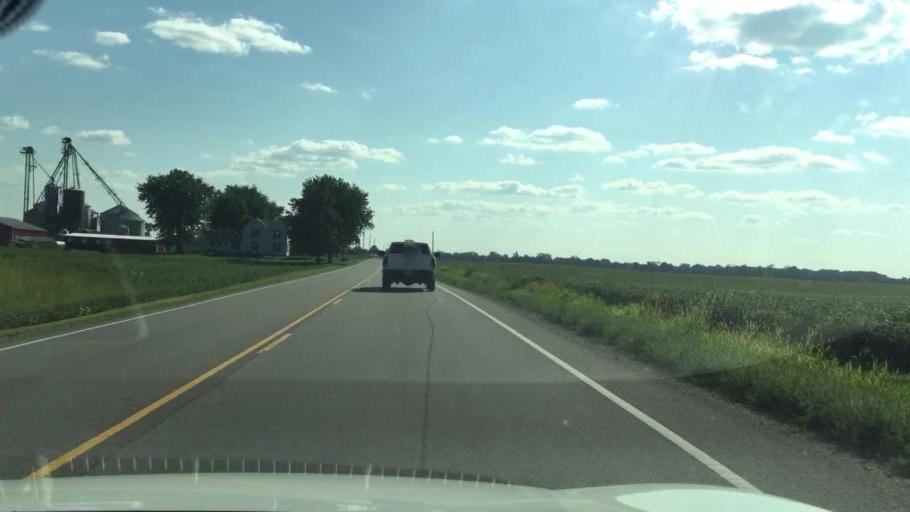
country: US
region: Ohio
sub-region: Champaign County
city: Mechanicsburg
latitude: 40.1431
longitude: -83.4732
